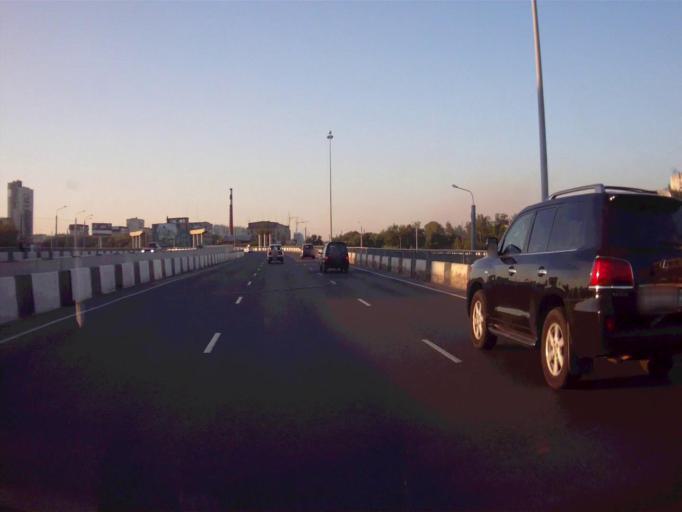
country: RU
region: Chelyabinsk
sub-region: Gorod Chelyabinsk
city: Chelyabinsk
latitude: 55.1705
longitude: 61.4151
